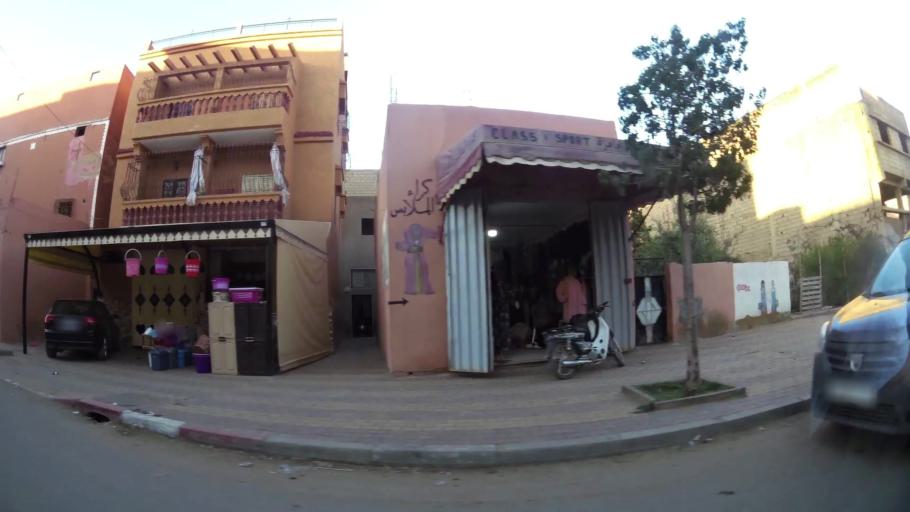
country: MA
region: Marrakech-Tensift-Al Haouz
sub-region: Kelaa-Des-Sraghna
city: Sidi Abdallah
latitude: 32.2420
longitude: -7.9541
